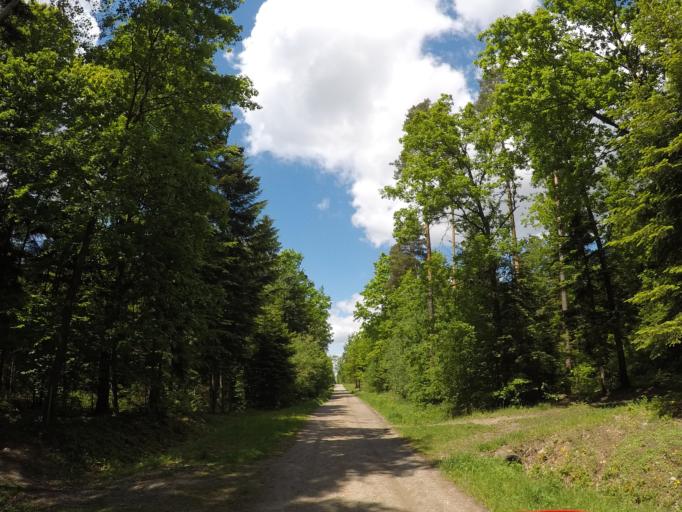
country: PL
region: Swietokrzyskie
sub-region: Powiat kielecki
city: Domaszowice
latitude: 50.9106
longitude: 20.6598
